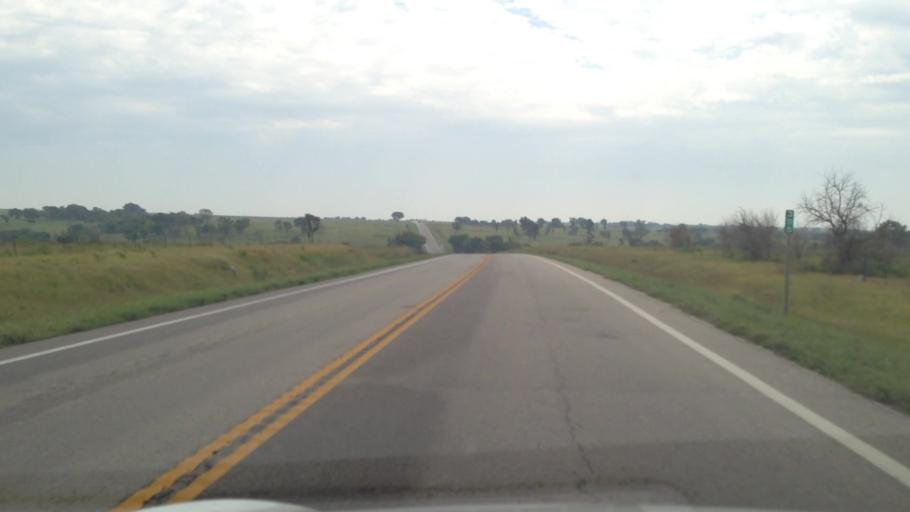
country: US
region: Kansas
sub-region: Bourbon County
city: Fort Scott
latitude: 37.8882
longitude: -95.0308
